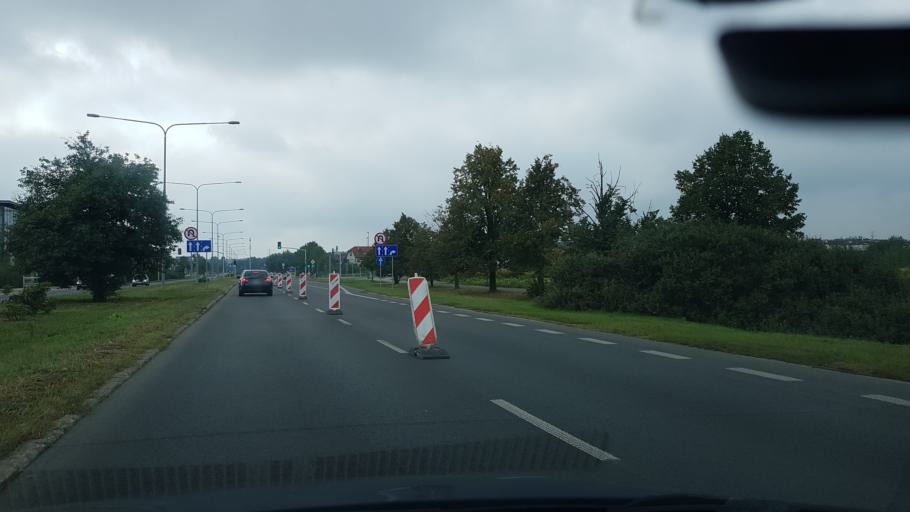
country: PL
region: Masovian Voivodeship
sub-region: Warszawa
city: Kabaty
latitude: 52.1323
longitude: 21.0990
